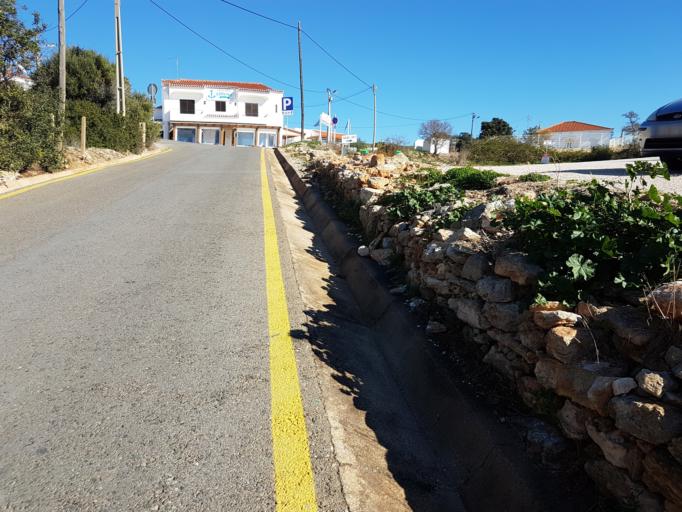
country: PT
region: Faro
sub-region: Lagoa
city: Carvoeiro
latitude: 37.0890
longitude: -8.4257
